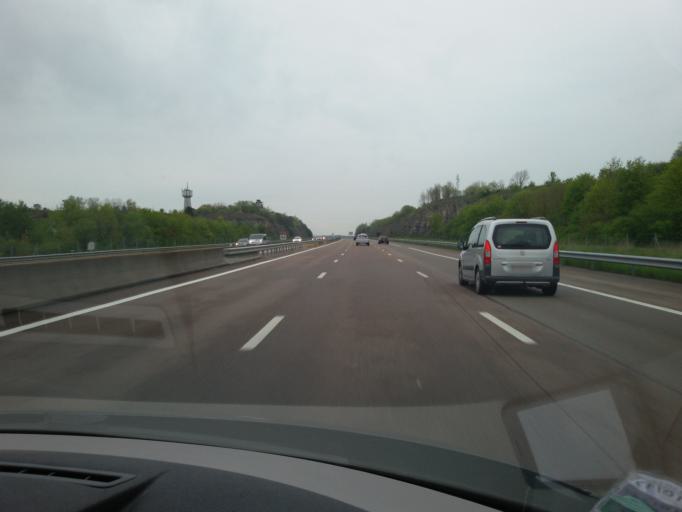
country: FR
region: Bourgogne
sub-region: Departement de la Cote-d'Or
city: Marcilly-sur-Tille
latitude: 47.5207
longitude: 5.1981
